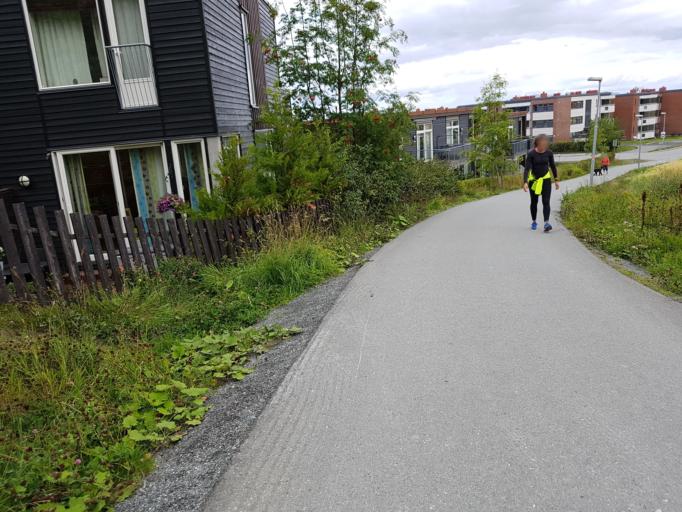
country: NO
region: Sor-Trondelag
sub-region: Trondheim
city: Trondheim
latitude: 63.4172
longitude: 10.4740
